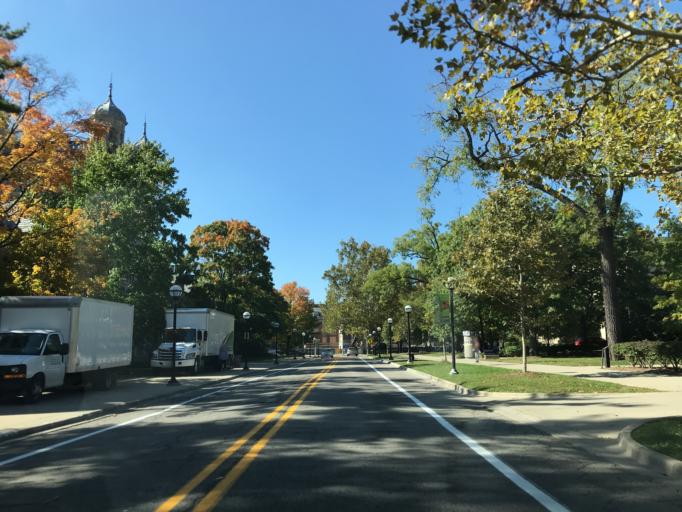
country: US
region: Michigan
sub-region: Washtenaw County
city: Ann Arbor
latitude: 42.2750
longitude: -83.7387
